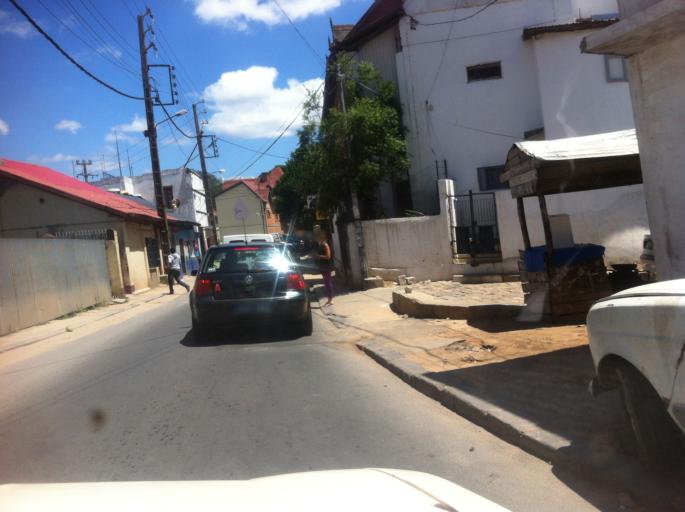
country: MG
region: Analamanga
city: Antananarivo
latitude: -18.9116
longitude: 47.5255
